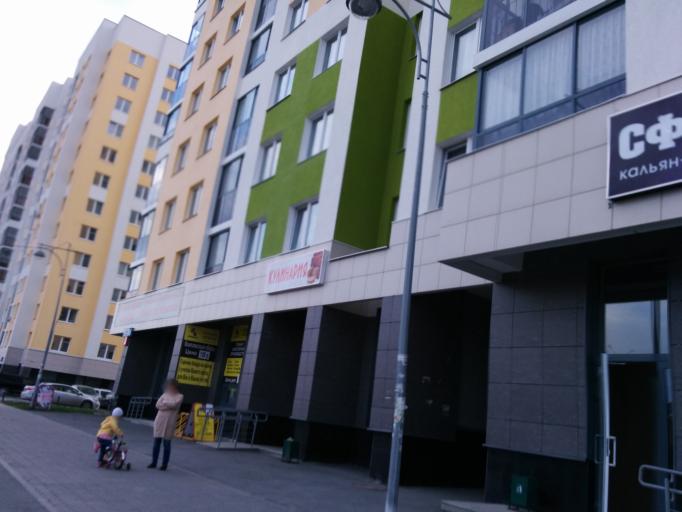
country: RU
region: Sverdlovsk
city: Sovkhoznyy
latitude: 56.7862
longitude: 60.5255
